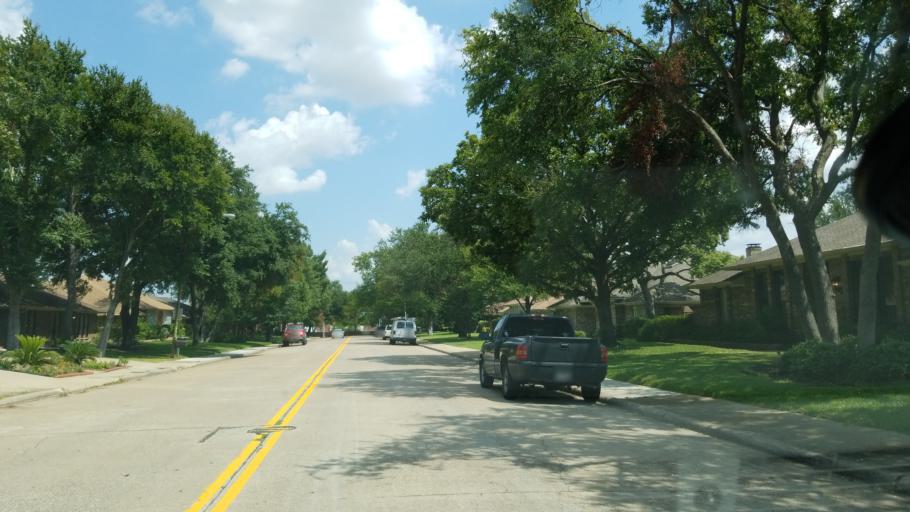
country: US
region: Texas
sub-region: Dallas County
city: Richardson
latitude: 32.9163
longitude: -96.7196
